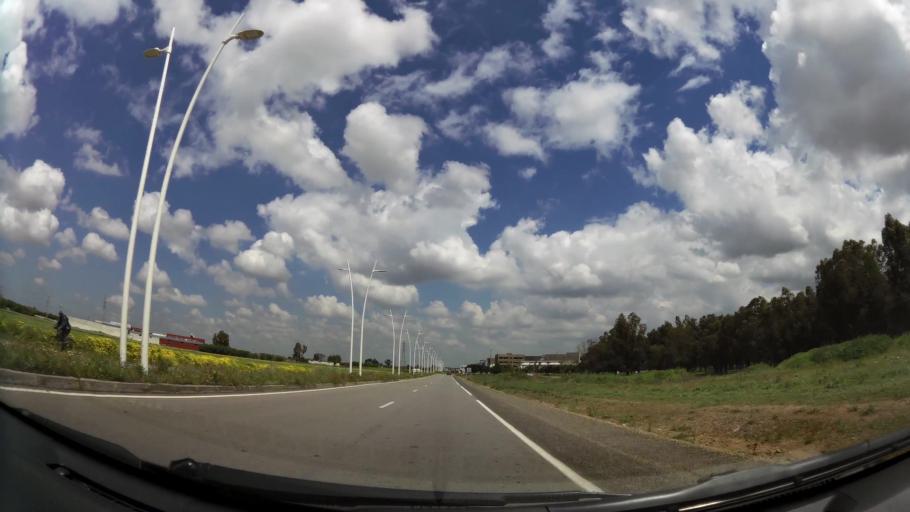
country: MA
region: Grand Casablanca
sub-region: Mediouna
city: Mediouna
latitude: 33.4037
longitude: -7.5590
